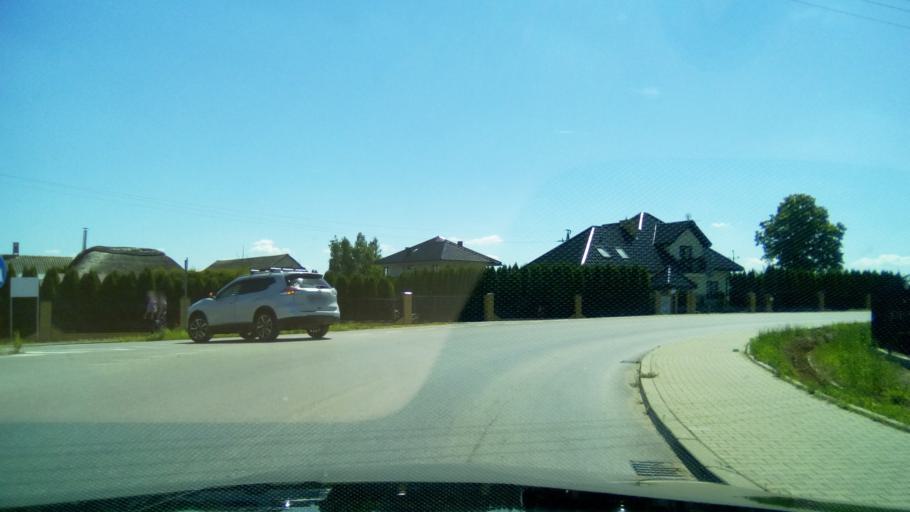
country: PL
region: Masovian Voivodeship
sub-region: Radom
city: Radom
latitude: 51.4299
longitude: 21.1187
